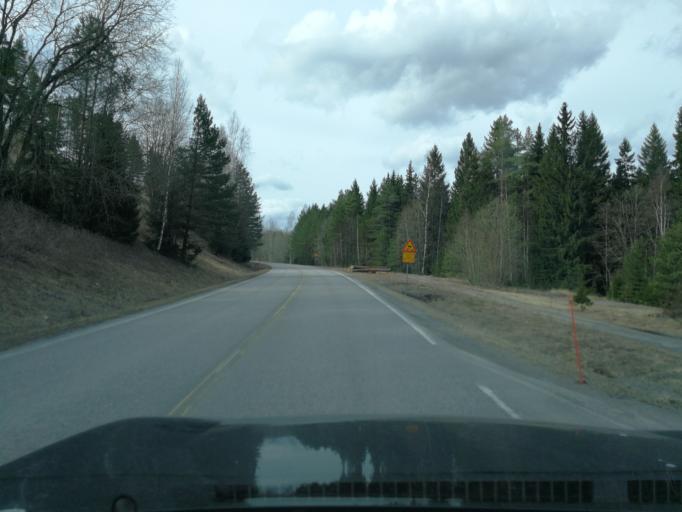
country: FI
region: Uusimaa
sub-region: Helsinki
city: Siuntio
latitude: 60.1914
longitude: 24.2015
